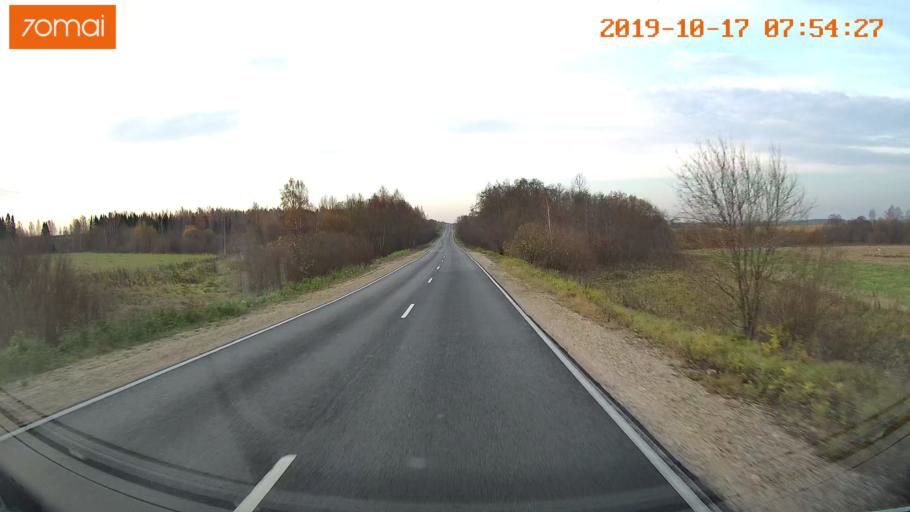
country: RU
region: Vladimir
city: Bavleny
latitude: 56.4494
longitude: 39.6064
